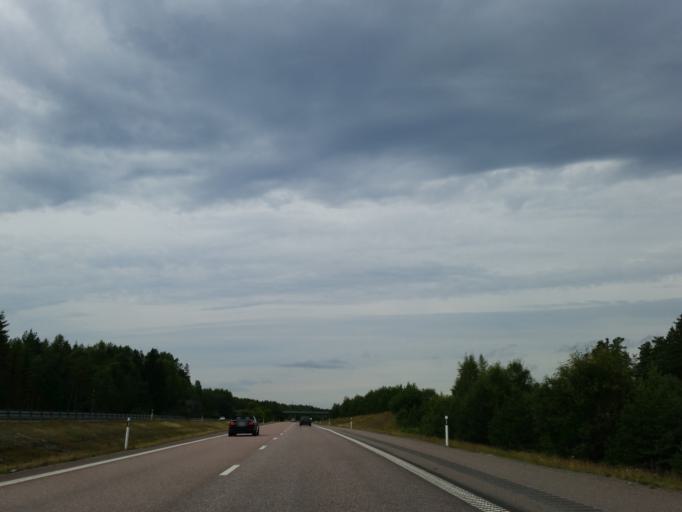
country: SE
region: Soedermanland
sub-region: Strangnas Kommun
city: Mariefred
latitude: 59.2277
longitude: 17.2233
